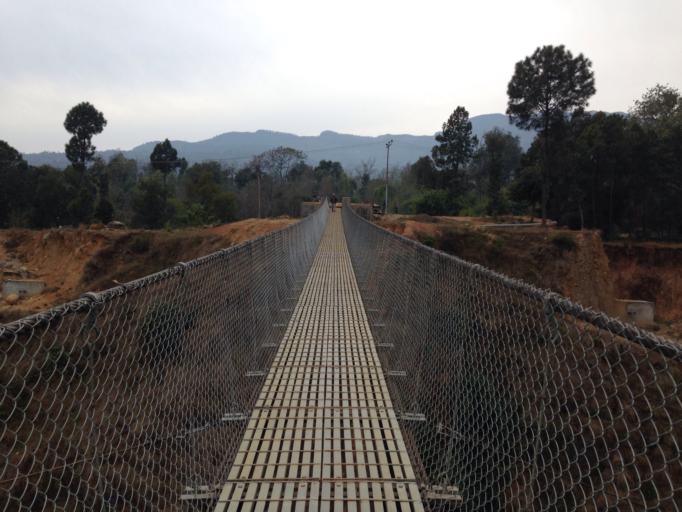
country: NP
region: Western Region
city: Baglung
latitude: 28.2049
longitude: 83.6698
